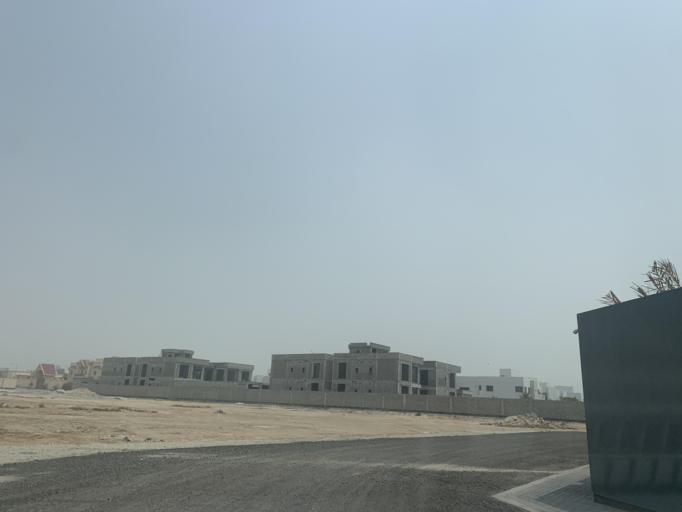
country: BH
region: Central Governorate
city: Madinat Hamad
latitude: 26.1660
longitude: 50.4749
